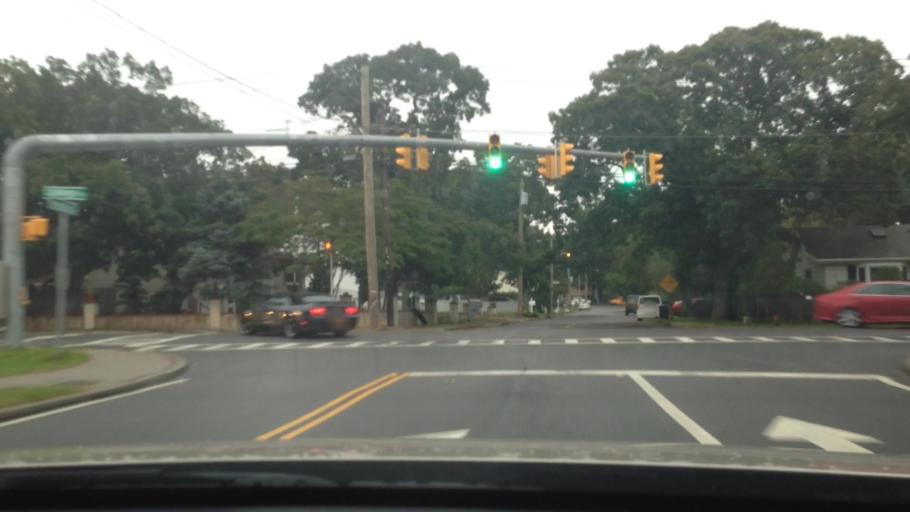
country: US
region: New York
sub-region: Suffolk County
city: Holtsville
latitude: 40.8403
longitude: -73.0551
